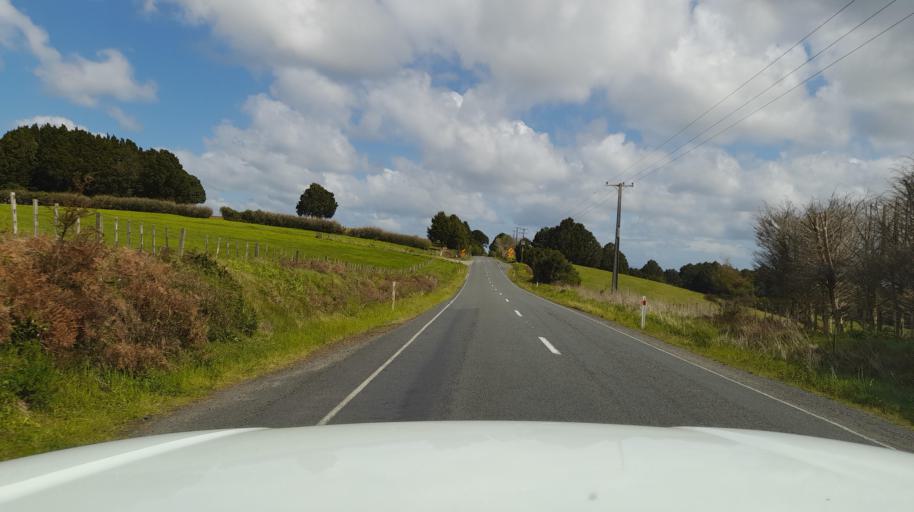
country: NZ
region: Northland
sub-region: Far North District
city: Waimate North
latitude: -35.2932
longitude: 173.8223
